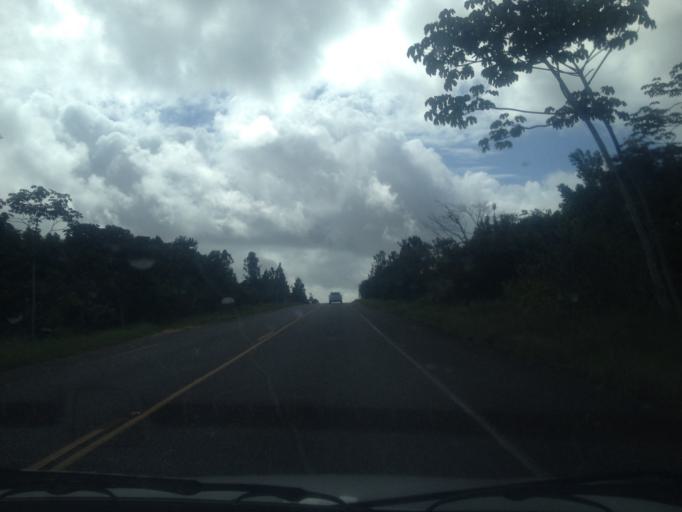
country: BR
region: Bahia
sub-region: Entre Rios
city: Entre Rios
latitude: -12.1658
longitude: -37.8084
